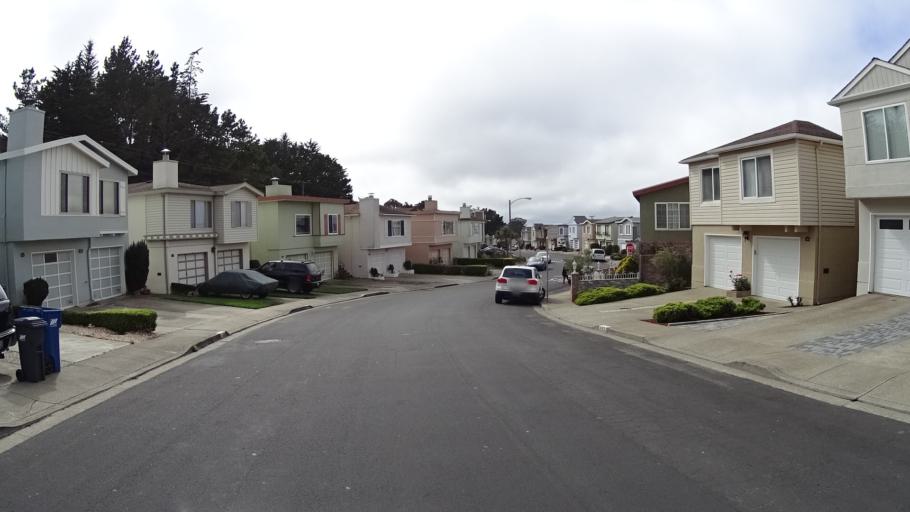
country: US
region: California
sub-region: San Mateo County
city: Daly City
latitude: 37.7045
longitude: -122.4378
